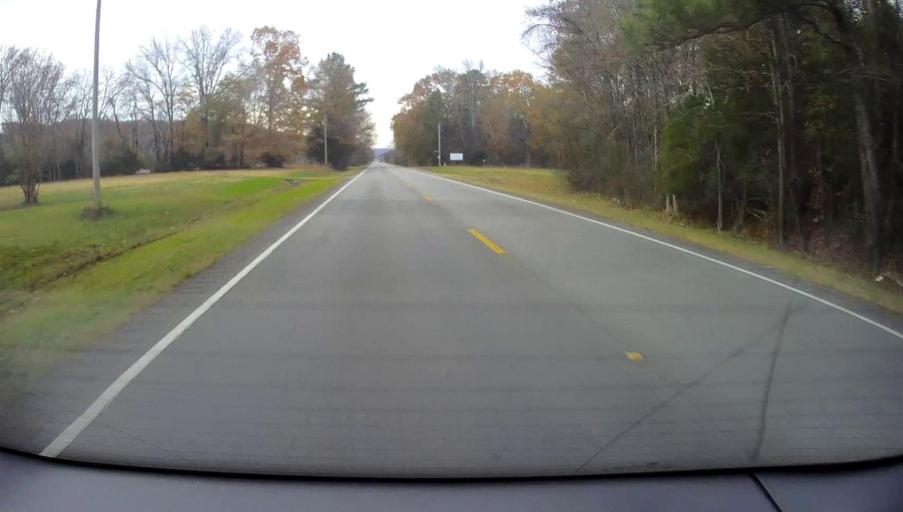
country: US
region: Alabama
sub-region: Marshall County
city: Arab
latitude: 34.3928
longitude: -86.6727
